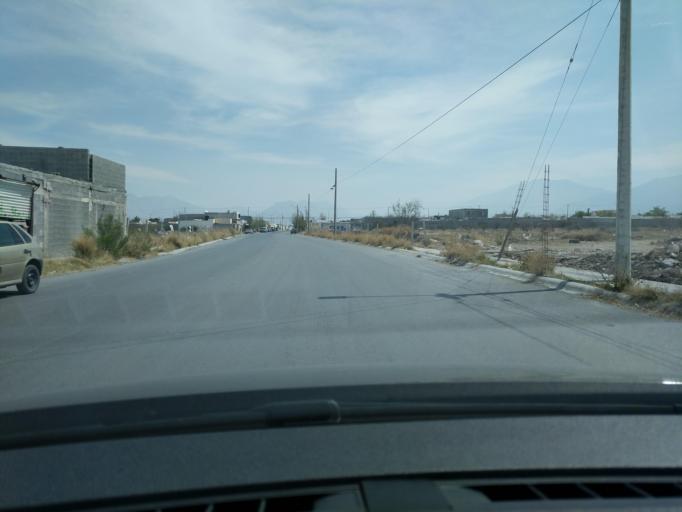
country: MX
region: Coahuila
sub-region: Arteaga
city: Arteaga
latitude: 25.4288
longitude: -100.9062
